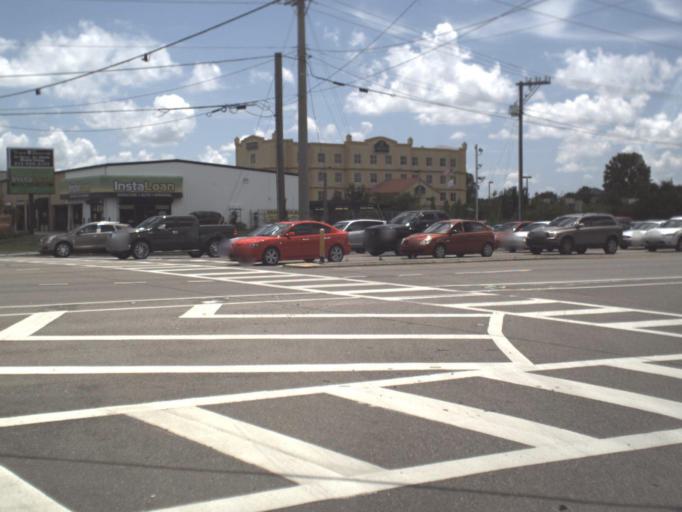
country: US
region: Florida
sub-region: Hillsborough County
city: Egypt Lake-Leto
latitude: 28.0257
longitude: -82.5051
